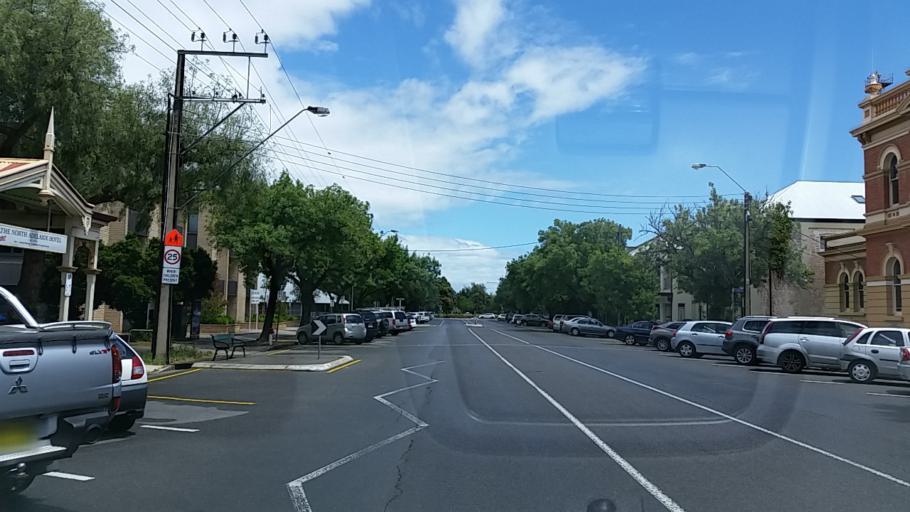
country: AU
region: South Australia
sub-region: Adelaide
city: North Adelaide
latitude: -34.9063
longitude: 138.5942
